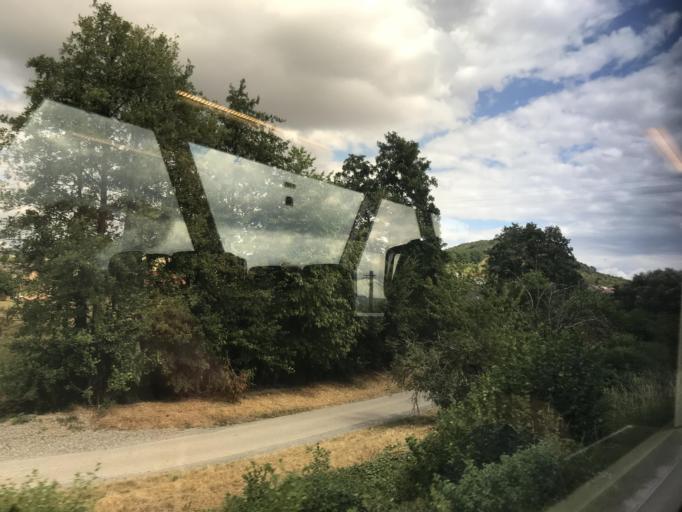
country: DE
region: Bavaria
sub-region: Regierungsbezirk Unterfranken
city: Hammelburg
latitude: 50.1277
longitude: 9.8324
